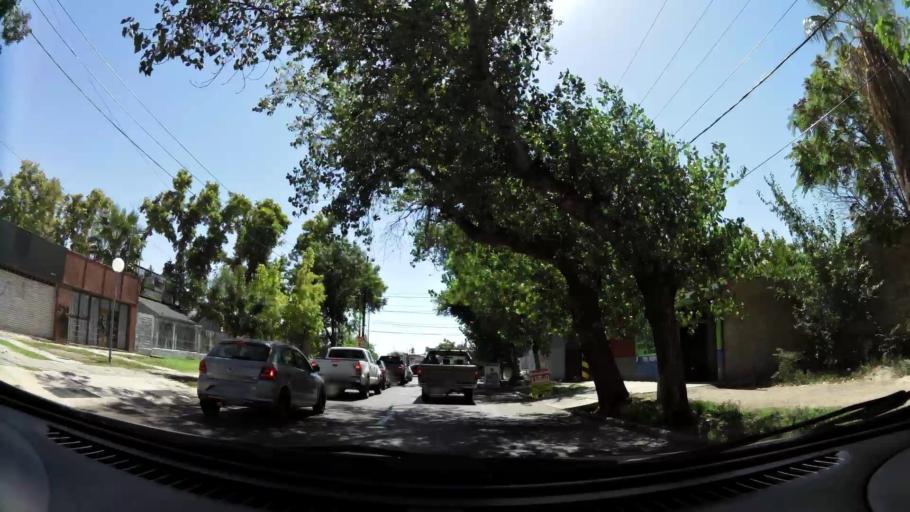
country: AR
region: Mendoza
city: Mendoza
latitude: -32.8951
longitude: -68.8178
